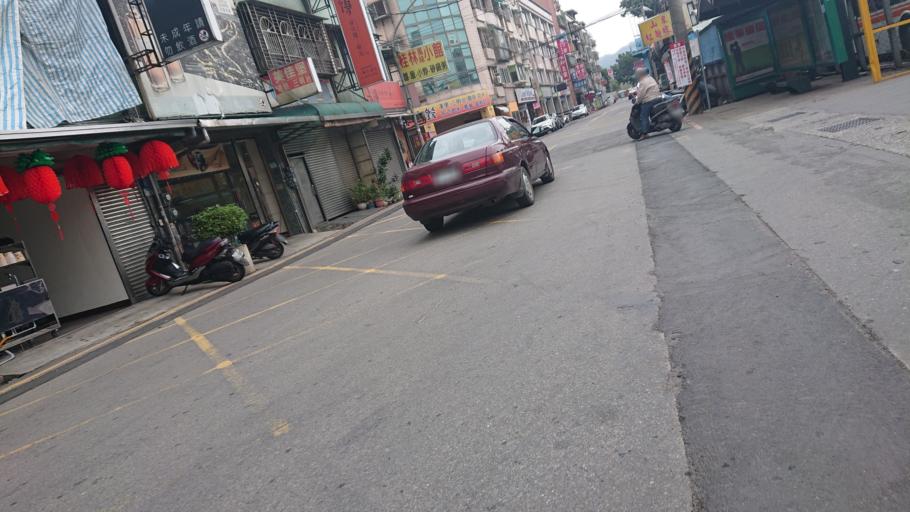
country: TW
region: Taiwan
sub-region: Taoyuan
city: Taoyuan
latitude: 24.9373
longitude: 121.3671
